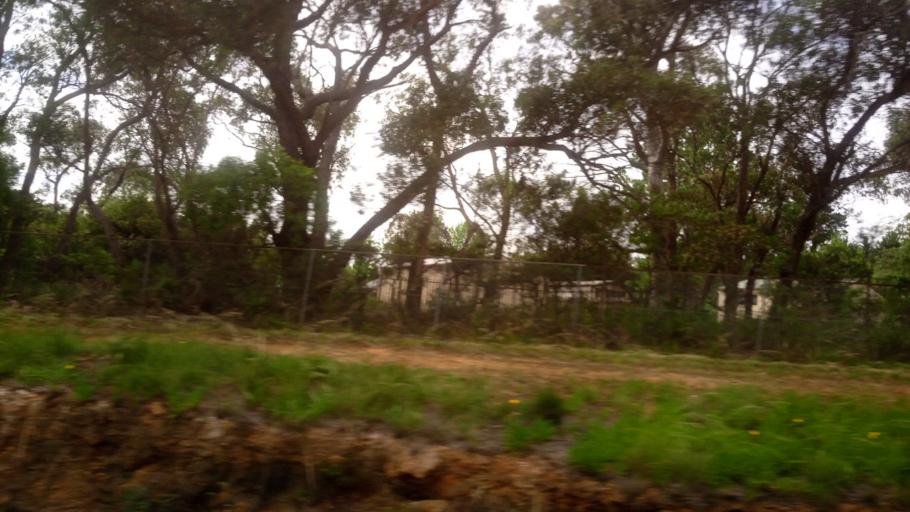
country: AU
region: New South Wales
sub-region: Blue Mountains Municipality
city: Leura
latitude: -33.7098
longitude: 150.3643
